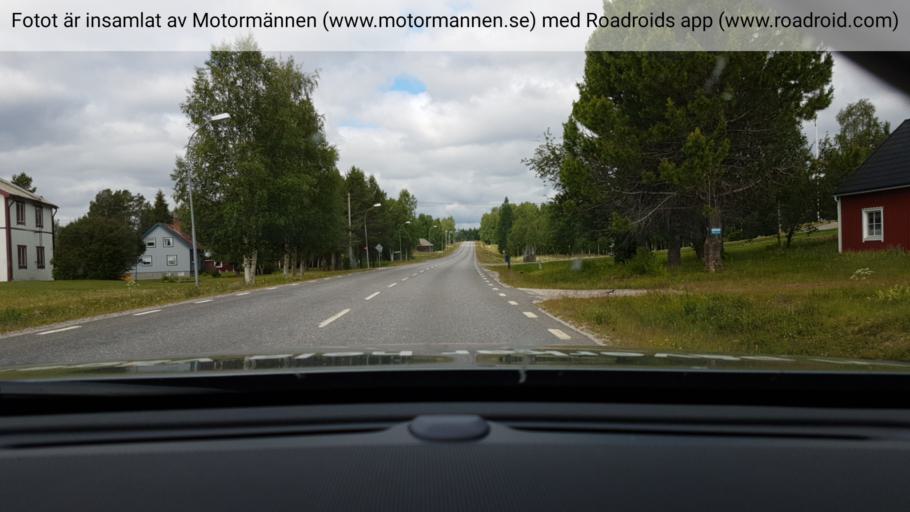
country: SE
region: Vaesterbotten
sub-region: Mala Kommun
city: Mala
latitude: 64.9876
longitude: 18.5084
